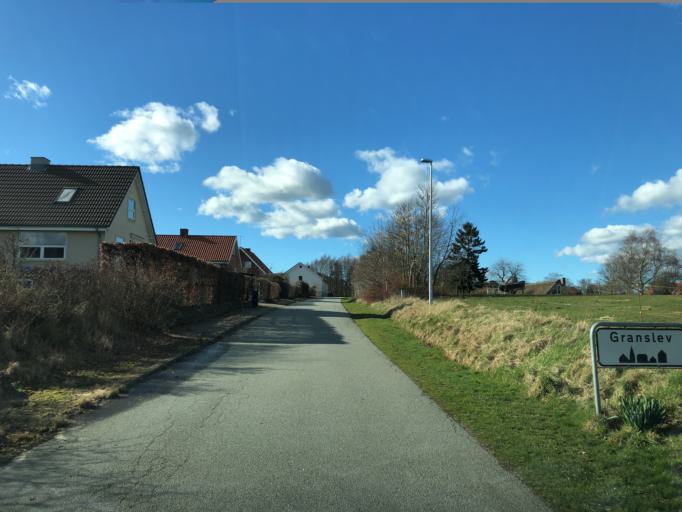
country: DK
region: Central Jutland
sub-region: Randers Kommune
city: Langa
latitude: 56.3257
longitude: 9.9118
